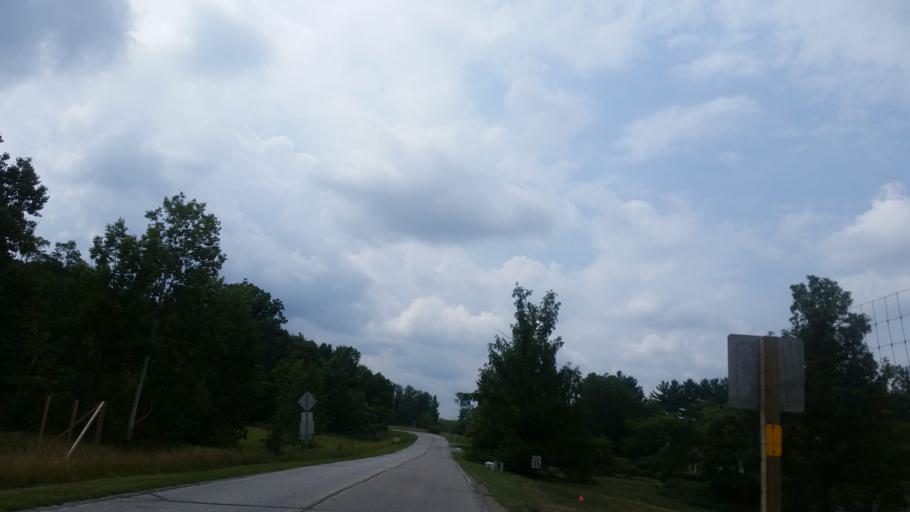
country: US
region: Ohio
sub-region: Lake County
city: Kirtland
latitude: 41.6154
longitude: -81.2984
